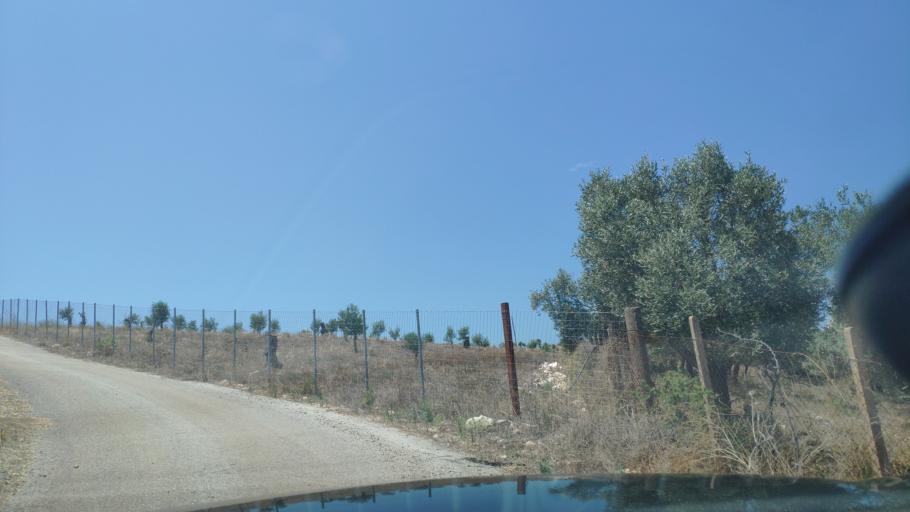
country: GR
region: West Greece
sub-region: Nomos Aitolias kai Akarnanias
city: Amfilochia
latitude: 38.9075
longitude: 21.1029
